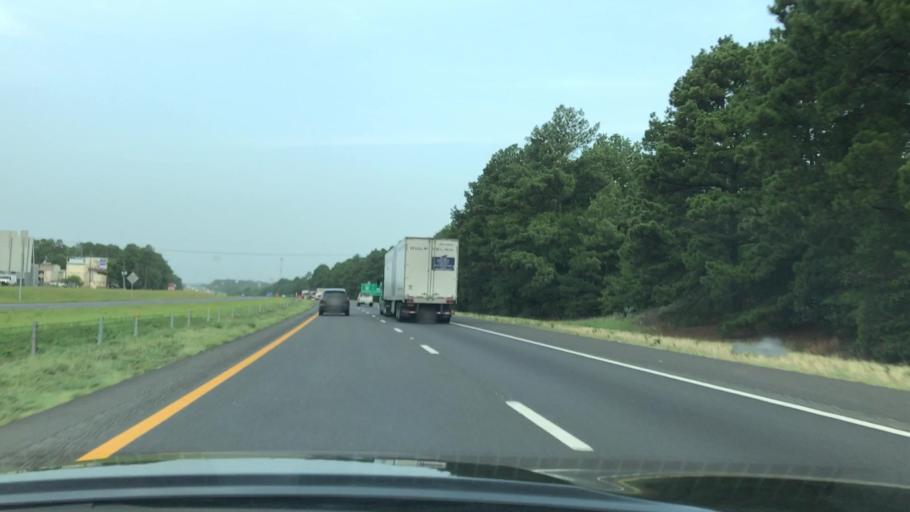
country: US
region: Texas
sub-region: Gregg County
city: Longview
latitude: 32.4573
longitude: -94.6872
